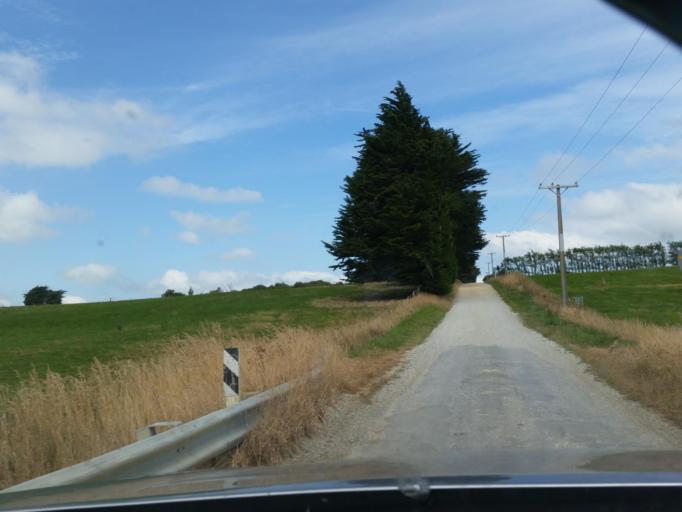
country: NZ
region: Southland
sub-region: Invercargill City
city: Invercargill
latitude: -46.3170
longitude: 168.4788
